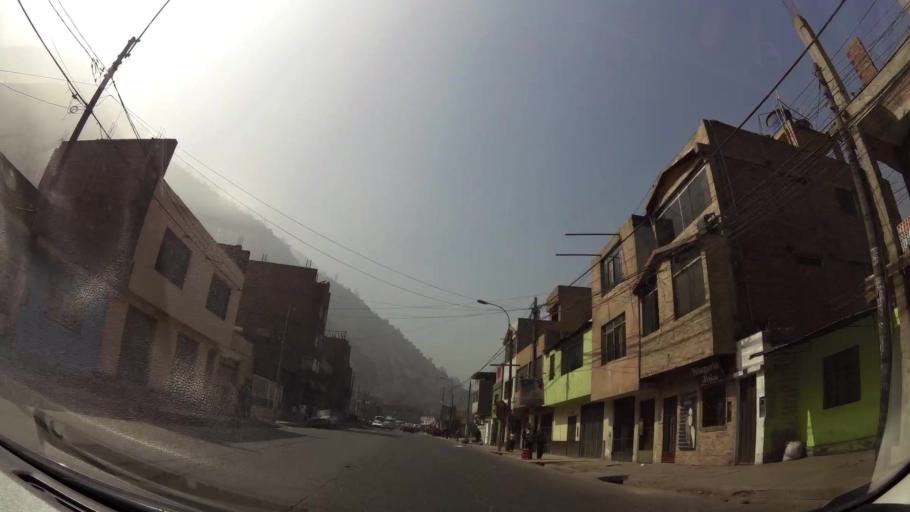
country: PE
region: Lima
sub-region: Lima
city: Asentamiento Humano Nicolas de Pierola
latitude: -11.9258
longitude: -76.6859
